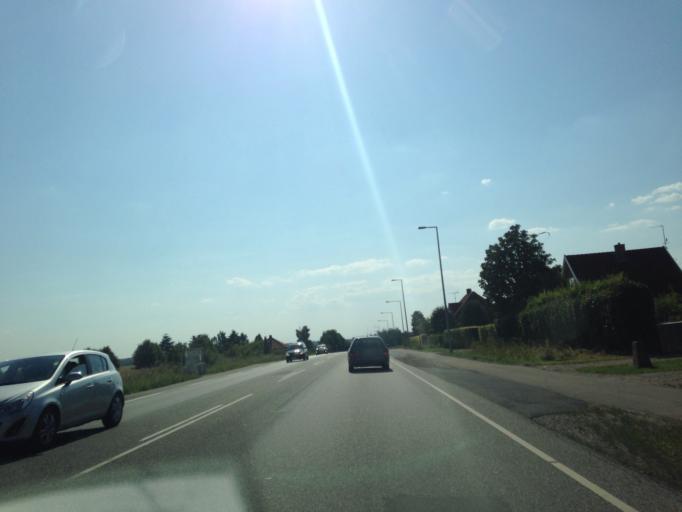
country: DK
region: Zealand
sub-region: Ringsted Kommune
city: Ringsted
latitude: 55.4819
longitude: 11.8441
